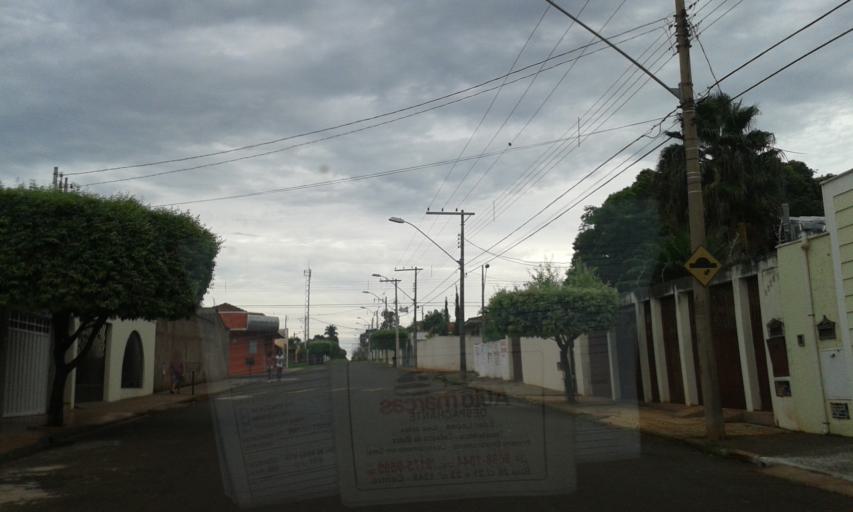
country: BR
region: Minas Gerais
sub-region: Ituiutaba
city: Ituiutaba
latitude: -18.9844
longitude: -49.4587
